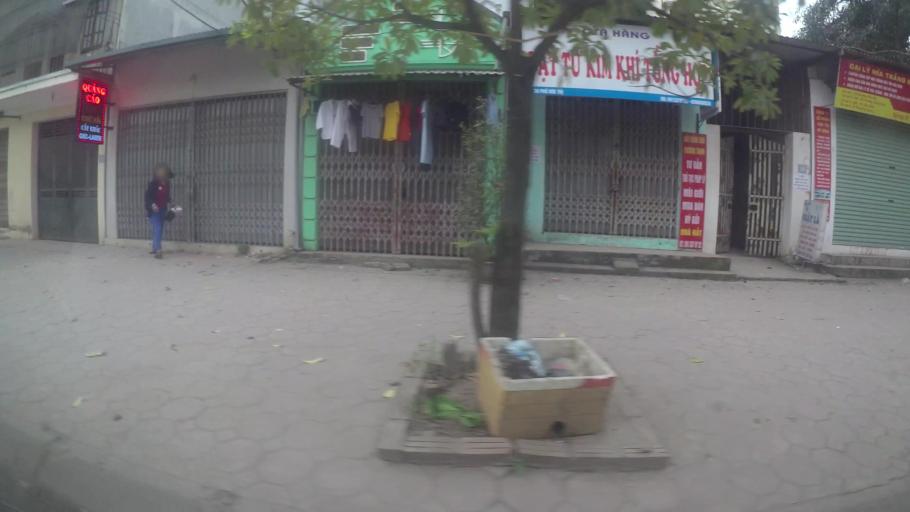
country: VN
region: Ha Noi
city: Cau Dien
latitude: 21.0366
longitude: 105.7412
